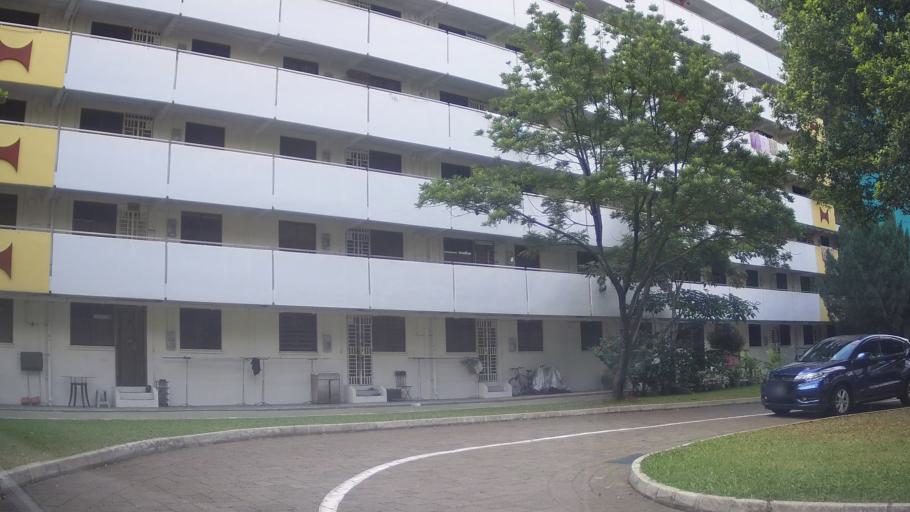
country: MY
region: Johor
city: Johor Bahru
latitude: 1.3364
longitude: 103.7241
